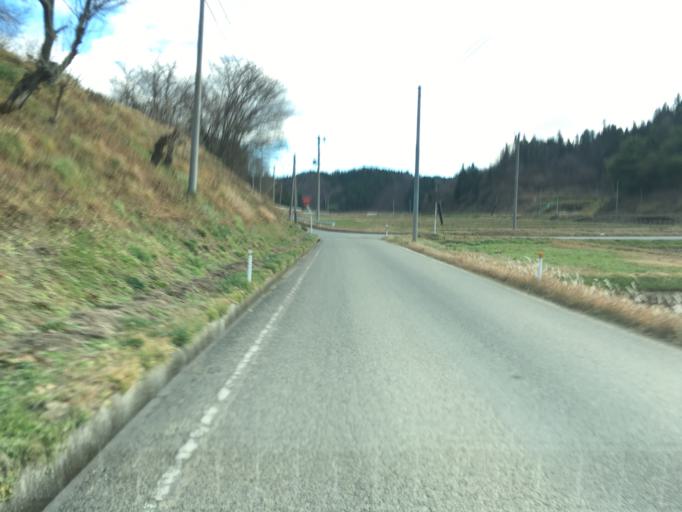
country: JP
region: Fukushima
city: Ishikawa
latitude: 37.2184
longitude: 140.5544
